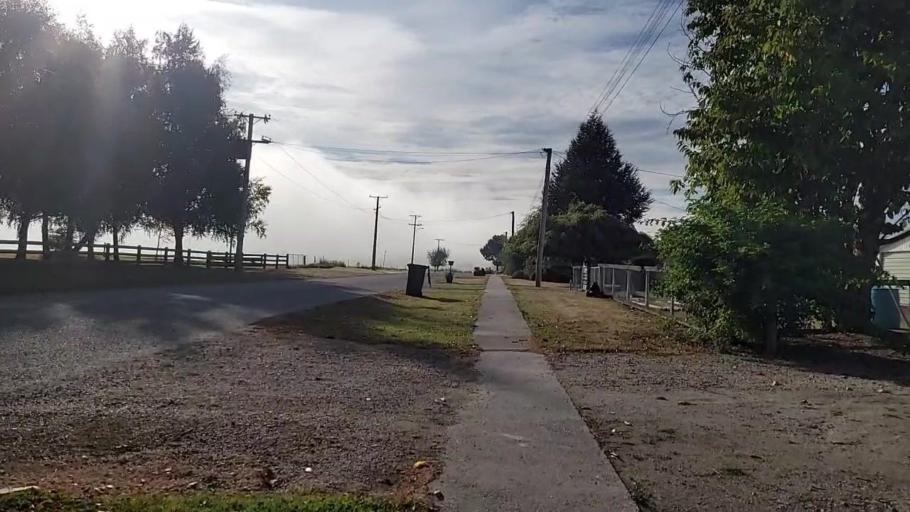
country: NZ
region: Southland
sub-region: Gore District
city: Gore
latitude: -45.6332
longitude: 169.3644
